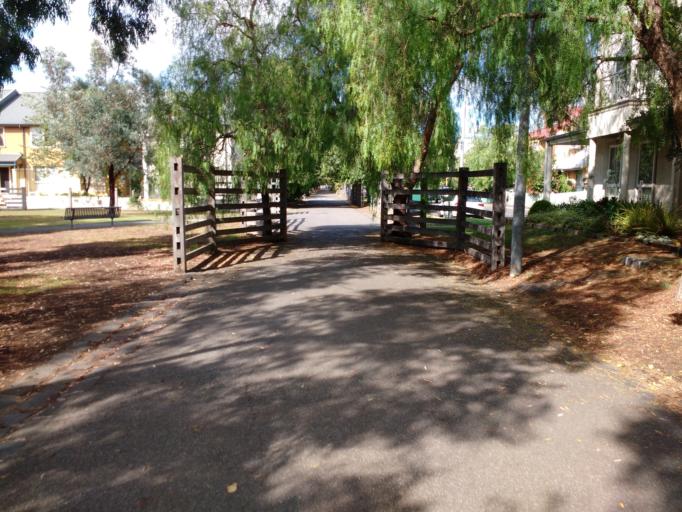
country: AU
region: Victoria
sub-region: Moonee Valley
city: Flemington
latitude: -37.7927
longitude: 144.9209
